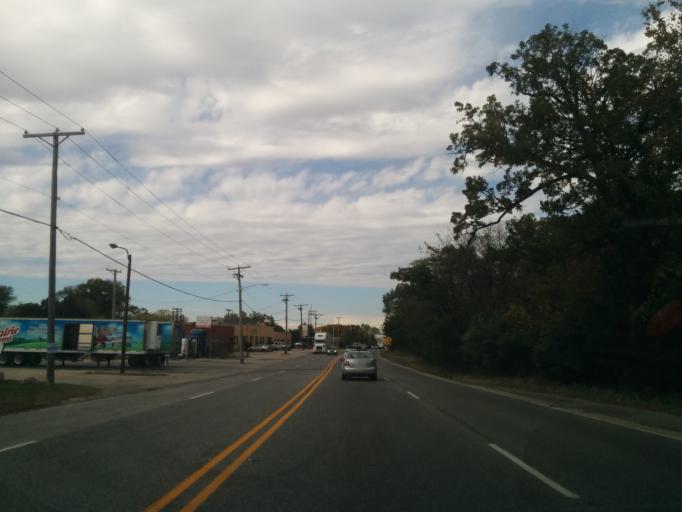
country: US
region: Illinois
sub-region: Cook County
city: Franklin Park
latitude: 41.9416
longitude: -87.8534
